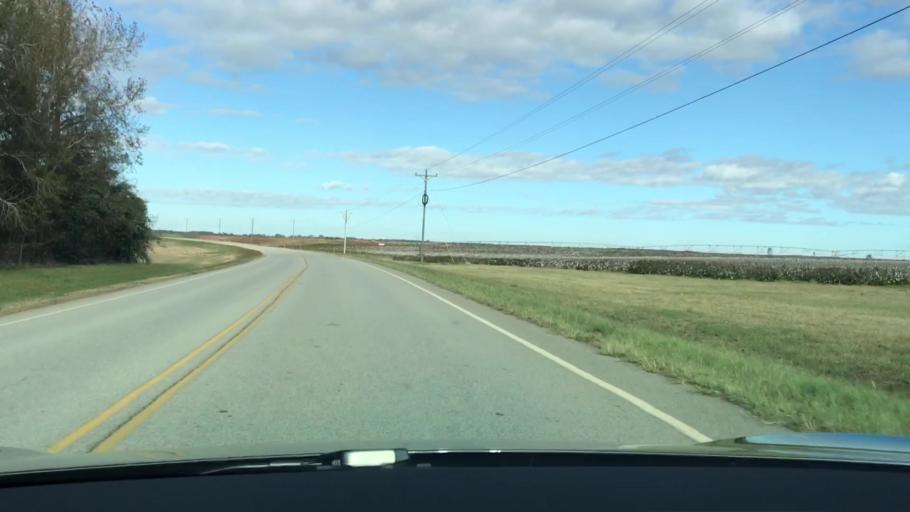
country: US
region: Georgia
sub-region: Jefferson County
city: Wrens
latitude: 33.1094
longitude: -82.4271
